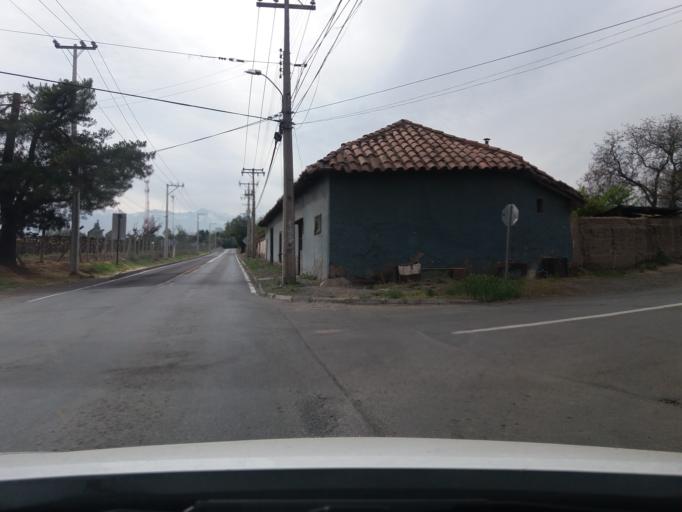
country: CL
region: Valparaiso
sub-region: Provincia de Los Andes
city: Los Andes
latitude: -32.8253
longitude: -70.6587
